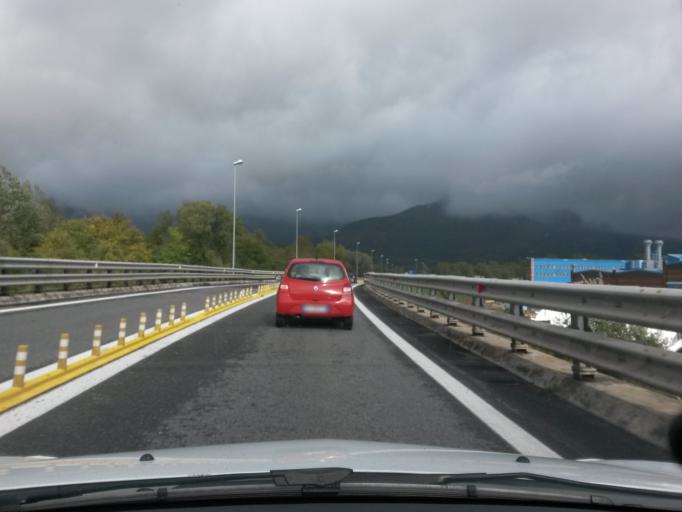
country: IT
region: Piedmont
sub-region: Provincia di Torino
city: Drubiaglio-Grangia
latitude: 45.0870
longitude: 7.4132
